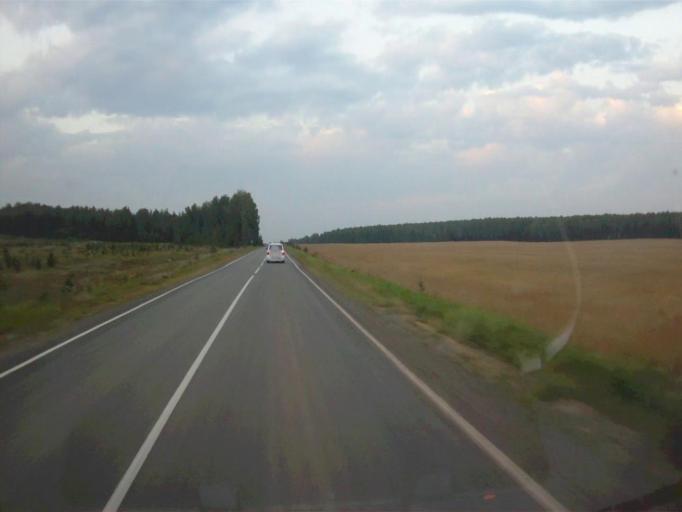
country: RU
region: Chelyabinsk
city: Chebarkul'
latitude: 55.1652
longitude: 60.4462
